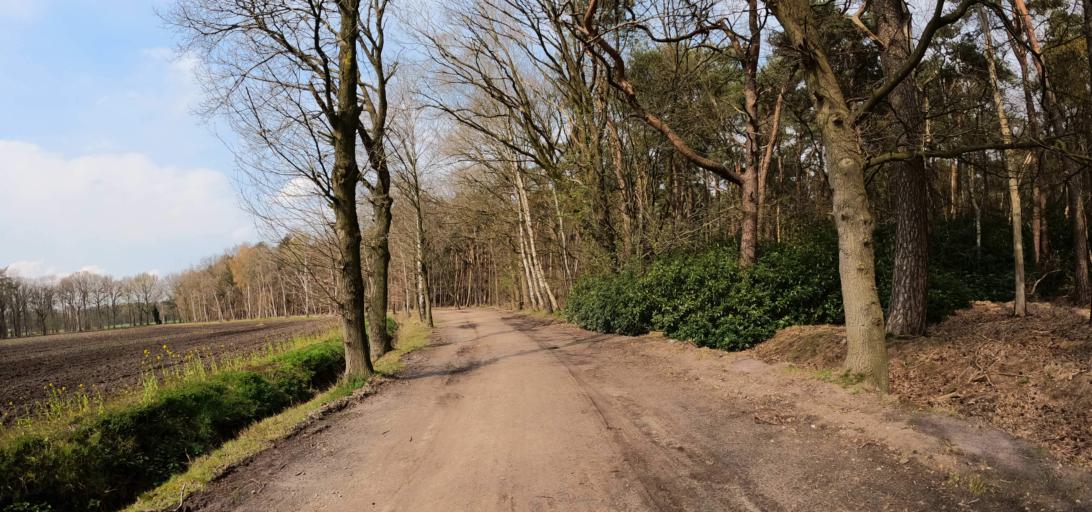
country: BE
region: Flanders
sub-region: Provincie Antwerpen
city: Kalmthout
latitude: 51.4232
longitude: 4.4396
